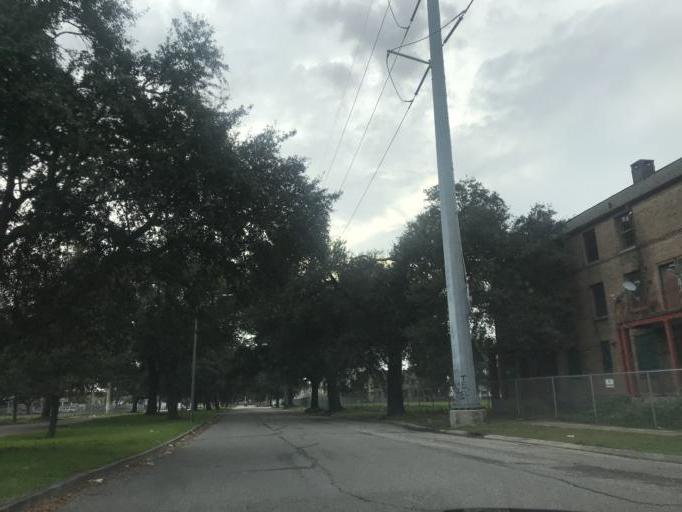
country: US
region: Louisiana
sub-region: Orleans Parish
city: New Orleans
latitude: 29.9519
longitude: -90.0911
